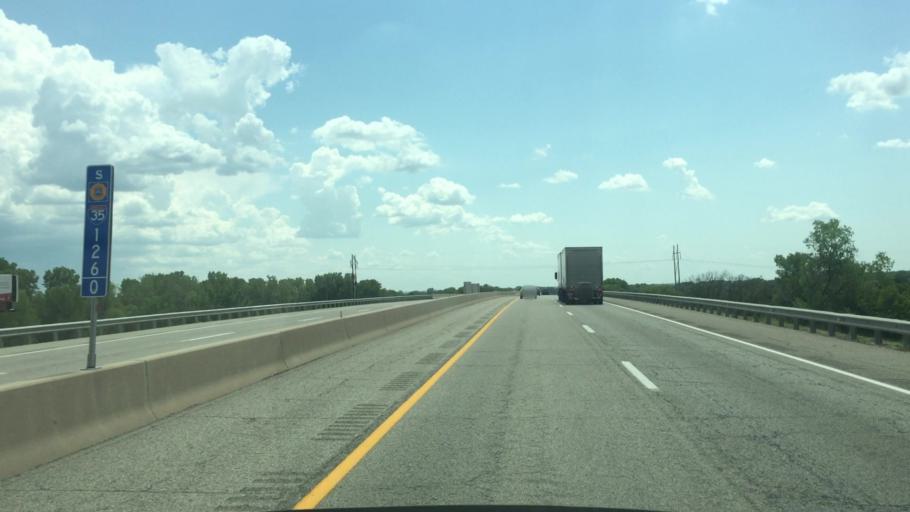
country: US
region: Kansas
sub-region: Lyon County
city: Emporia
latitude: 38.4032
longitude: -96.2460
